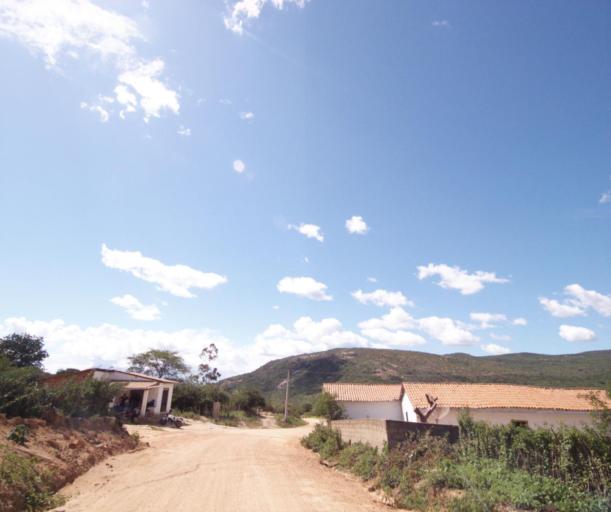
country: BR
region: Bahia
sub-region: Pocoes
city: Pocoes
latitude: -14.2528
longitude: -40.7052
